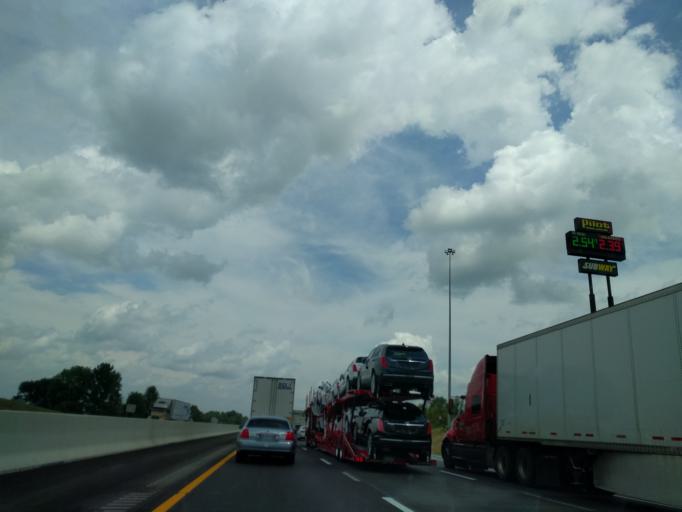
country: US
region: Kentucky
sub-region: Larue County
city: Hodgenville
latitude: 37.5238
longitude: -85.8843
